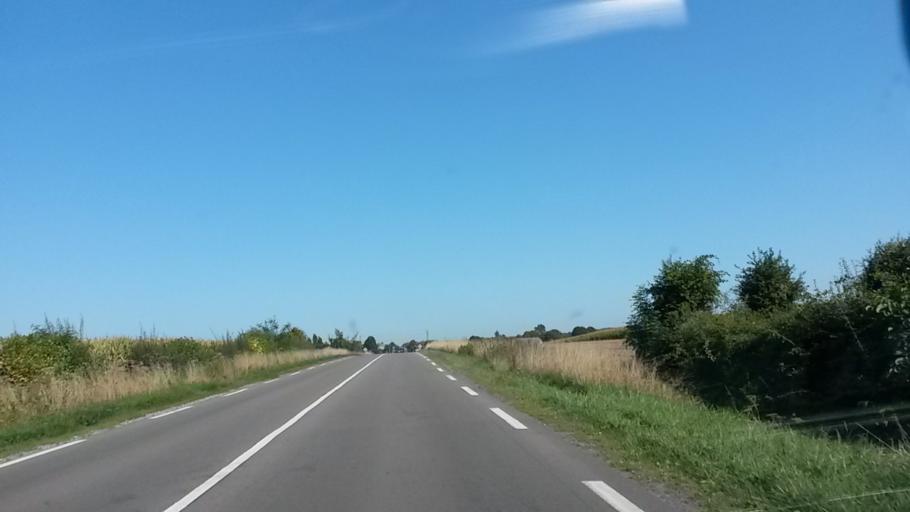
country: FR
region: Nord-Pas-de-Calais
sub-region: Departement du Nord
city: Avesnelles
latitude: 50.1709
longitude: 3.9534
